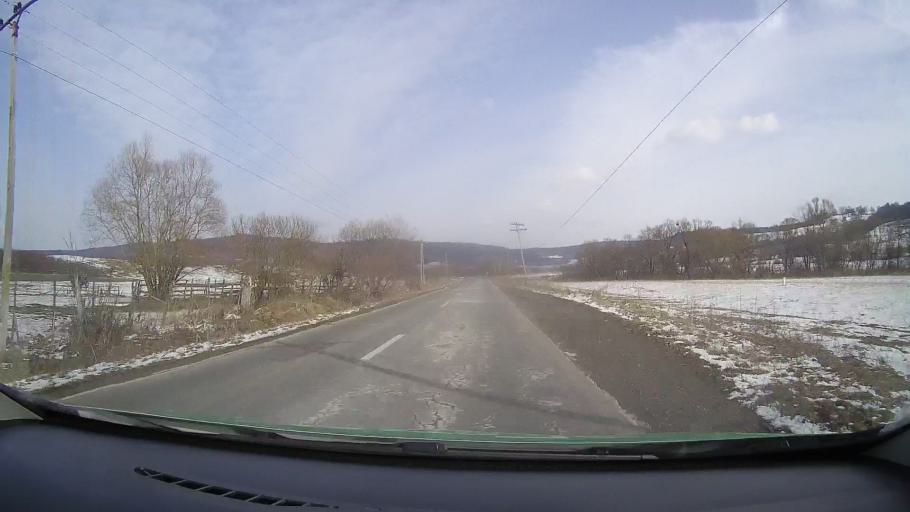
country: RO
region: Mures
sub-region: Comuna Apold
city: Saes
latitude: 46.1416
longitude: 24.7950
